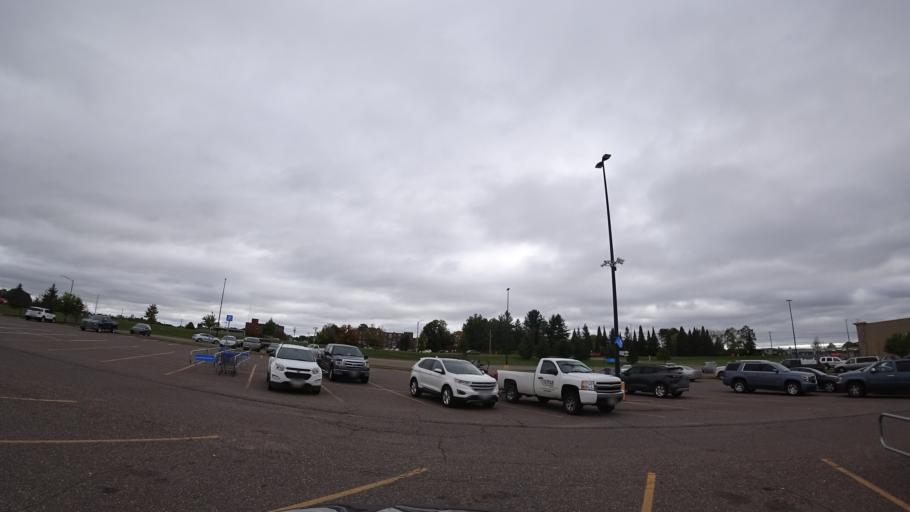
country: US
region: Wisconsin
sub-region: Rusk County
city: Ladysmith
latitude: 45.4574
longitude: -91.1125
